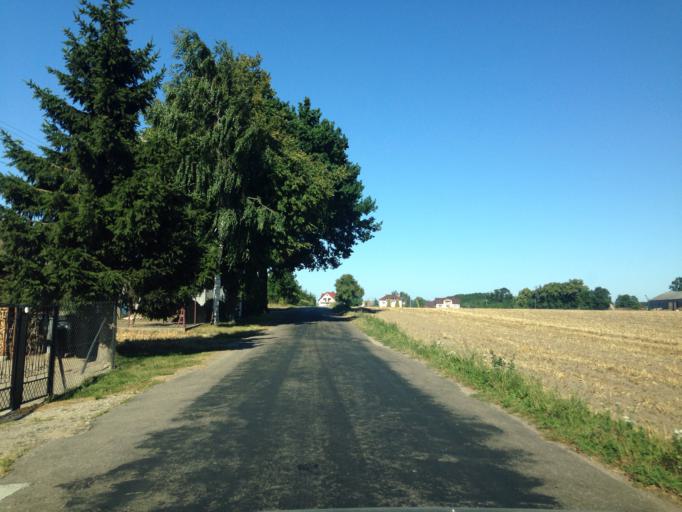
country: PL
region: Kujawsko-Pomorskie
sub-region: Powiat brodnicki
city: Swiedziebnia
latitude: 53.1988
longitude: 19.5416
